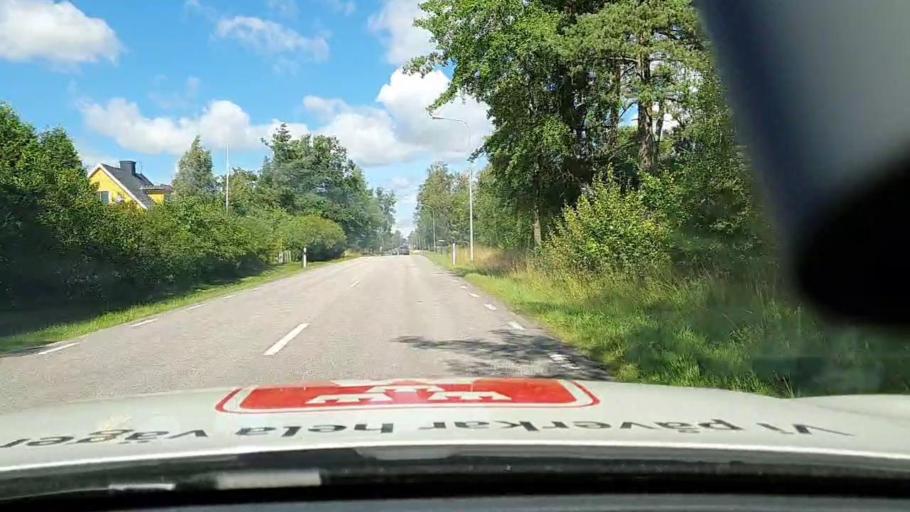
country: SE
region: Vaestra Goetaland
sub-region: Skovde Kommun
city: Stopen
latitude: 58.5604
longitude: 14.0074
